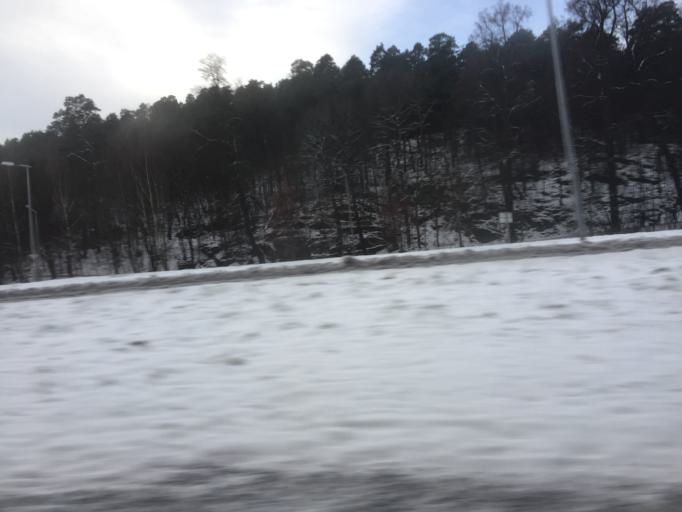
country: NO
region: Akershus
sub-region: Oppegard
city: Kolbotn
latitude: 59.8373
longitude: 10.7789
